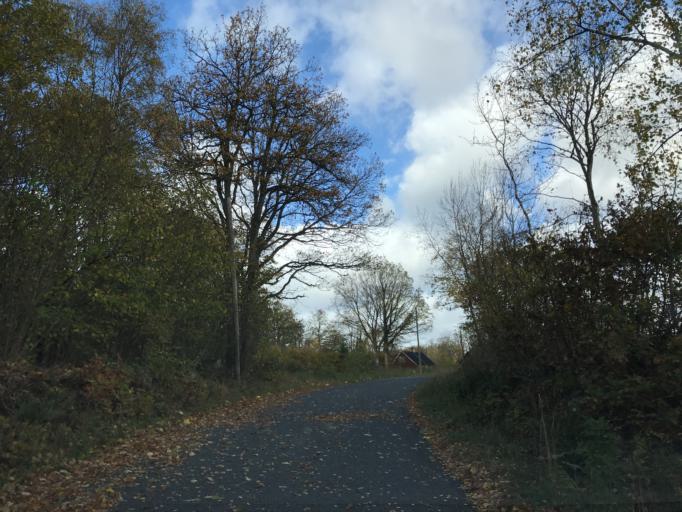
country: SE
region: Skane
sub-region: Perstorps Kommun
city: Perstorp
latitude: 56.0365
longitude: 13.3959
